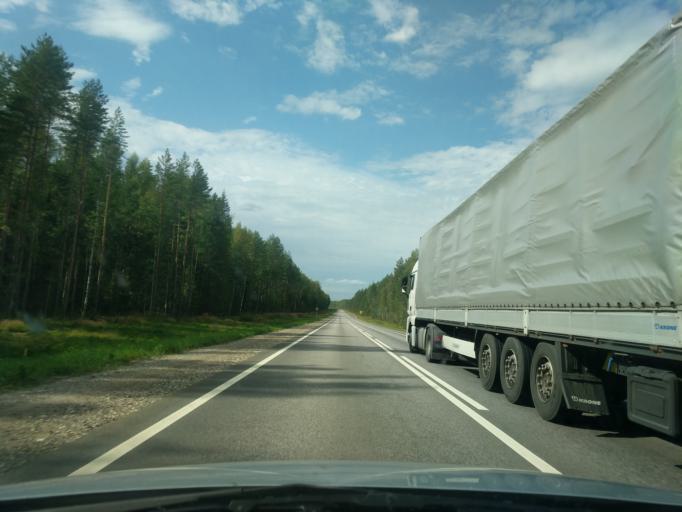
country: RU
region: Kostroma
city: Kadyy
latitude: 57.7993
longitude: 42.8233
